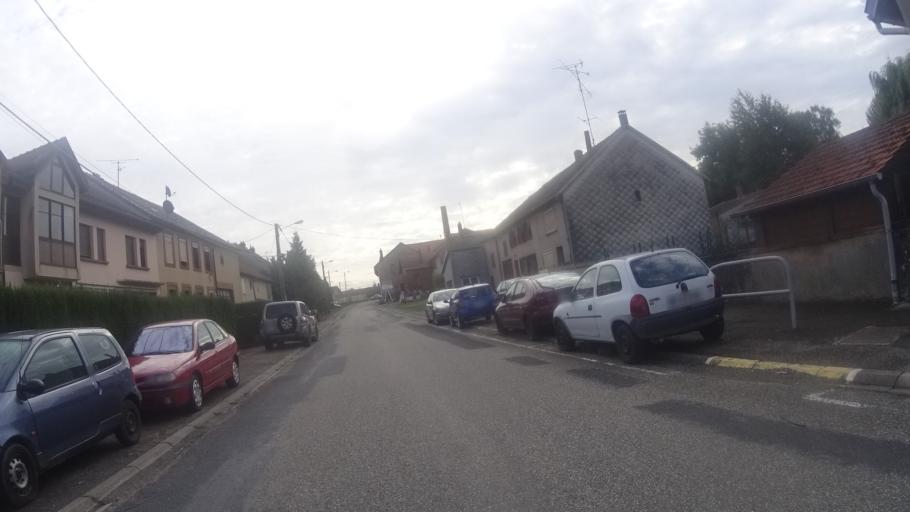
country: FR
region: Lorraine
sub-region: Departement de la Moselle
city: Niderviller
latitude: 48.7151
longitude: 7.1068
